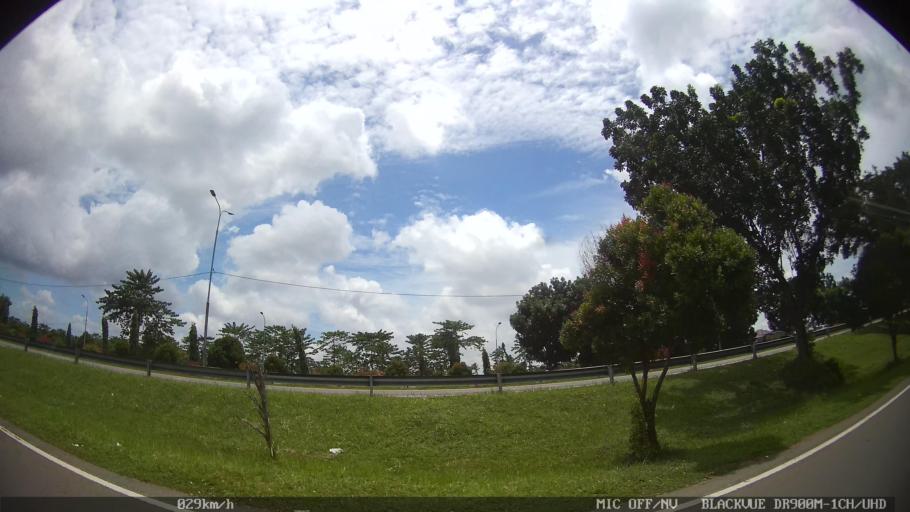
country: ID
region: North Sumatra
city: Medan
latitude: 3.5997
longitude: 98.7236
